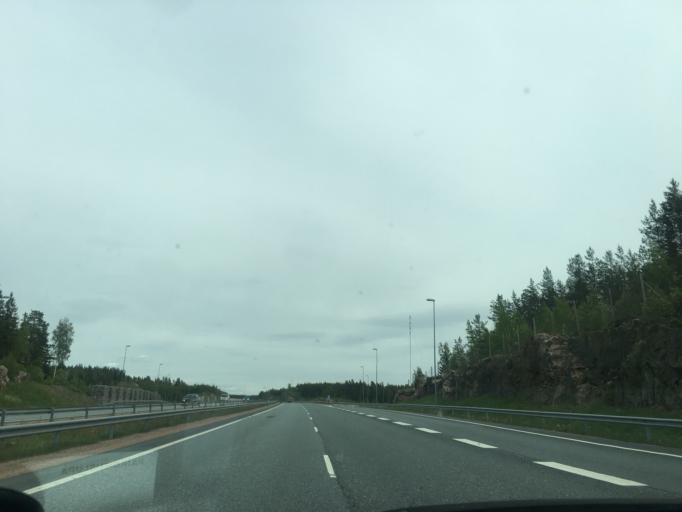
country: FI
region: Varsinais-Suomi
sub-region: Salo
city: Suomusjaervi
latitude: 60.3694
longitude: 23.7009
